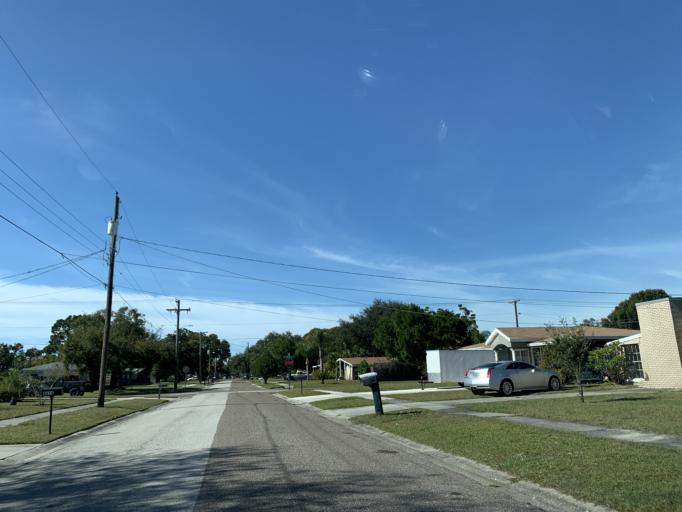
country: US
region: Florida
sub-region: Hillsborough County
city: Tampa
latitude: 27.8853
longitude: -82.5036
